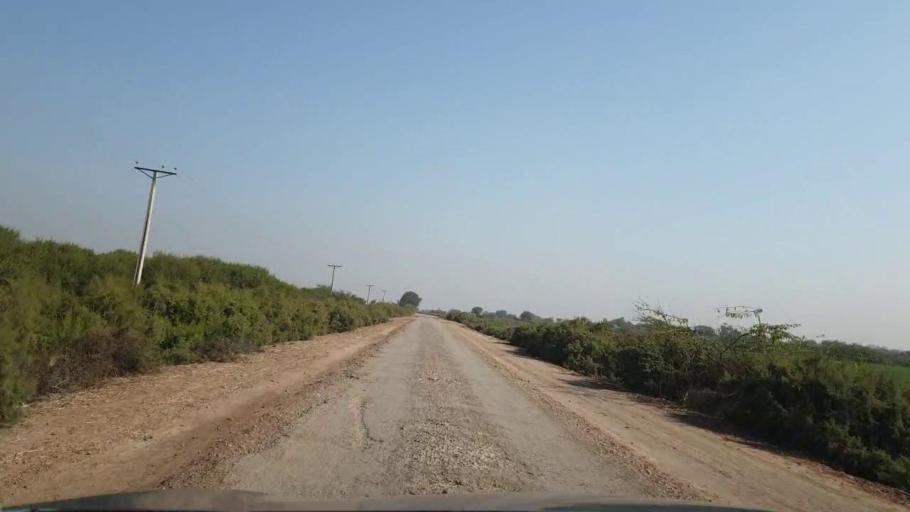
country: PK
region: Sindh
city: Berani
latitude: 25.6297
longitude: 68.8613
